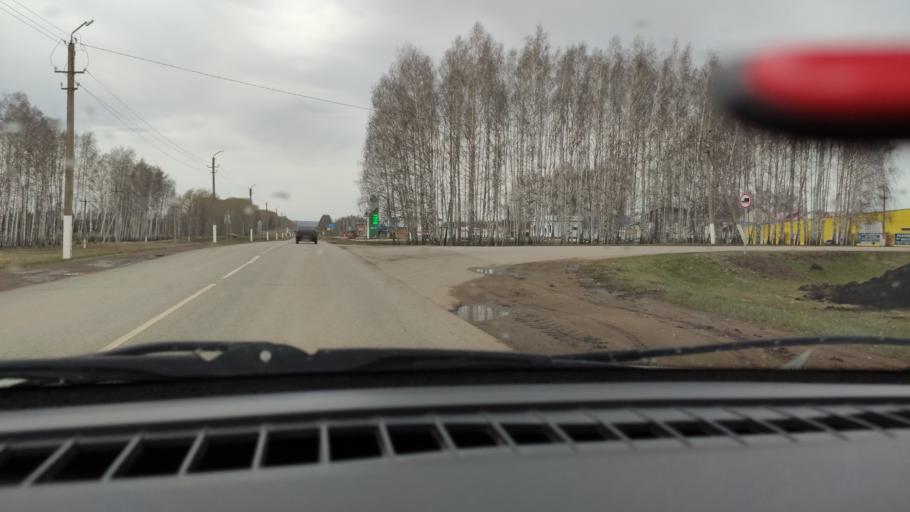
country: RU
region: Bashkortostan
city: Burayevo
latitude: 55.8326
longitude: 55.3991
